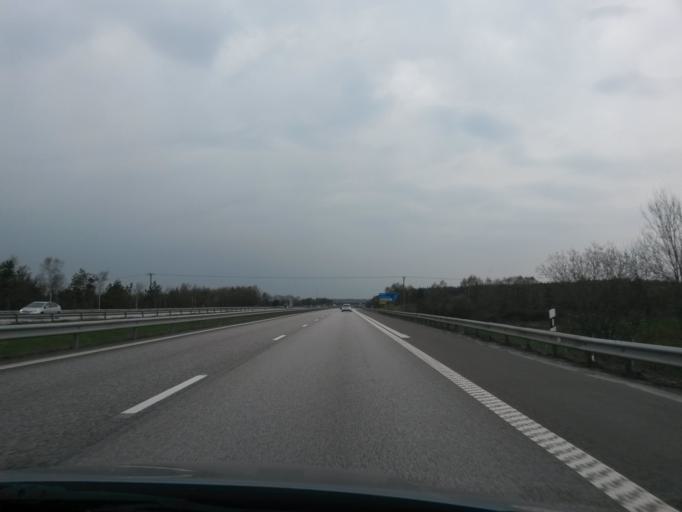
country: SE
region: Halland
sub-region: Kungsbacka Kommun
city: Frillesas
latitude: 57.2431
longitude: 12.2202
